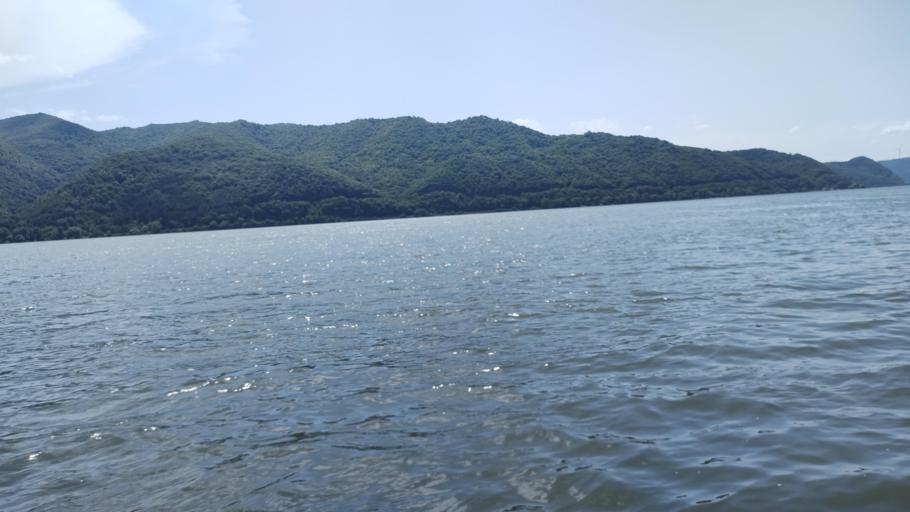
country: RO
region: Caras-Severin
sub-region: Comuna Berzasca
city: Liubcova
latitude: 44.6550
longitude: 21.8213
